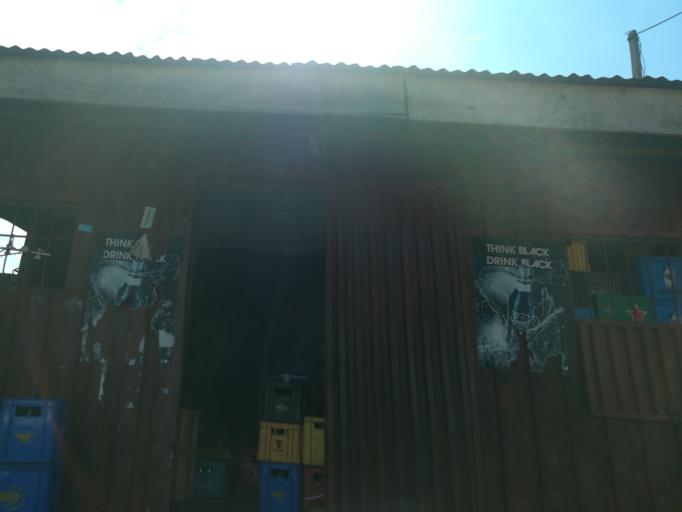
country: NG
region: Lagos
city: Ikorodu
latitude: 6.6014
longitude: 3.5027
